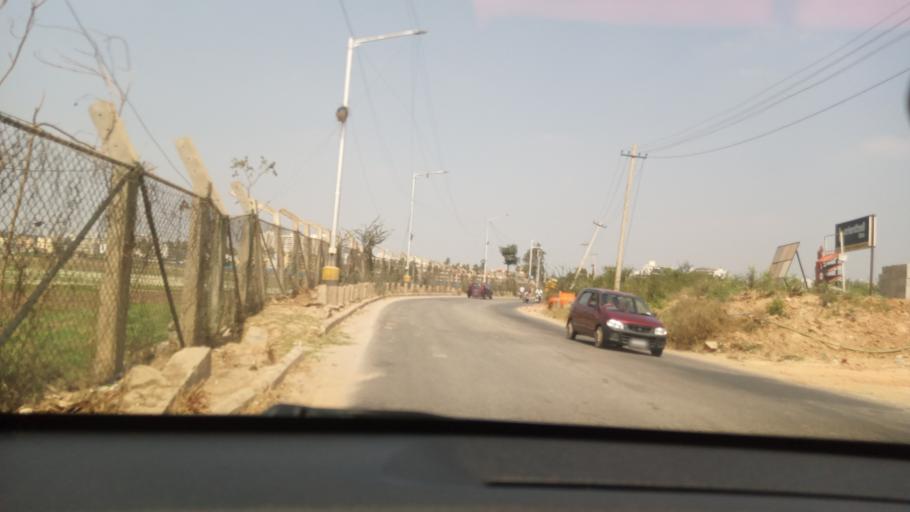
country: IN
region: Karnataka
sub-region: Bangalore Rural
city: Hoskote
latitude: 12.9499
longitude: 77.7451
